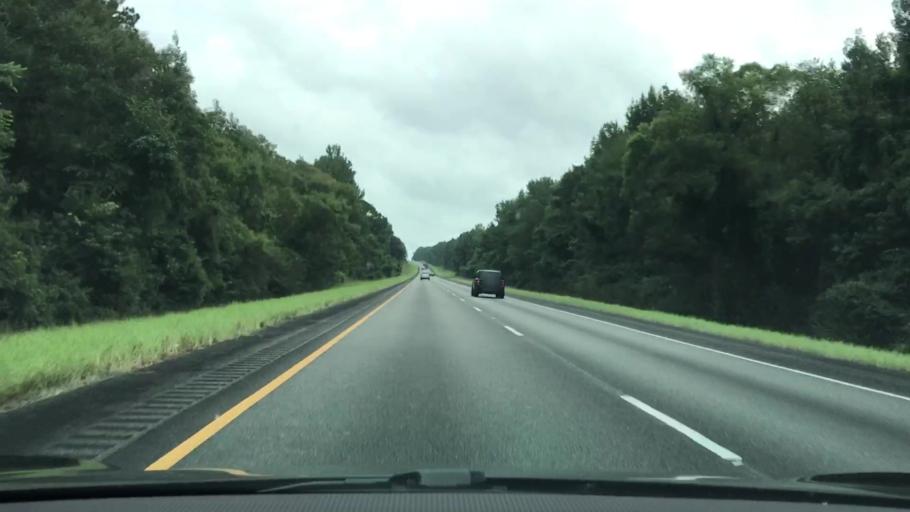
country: US
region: Alabama
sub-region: Elmore County
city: Tallassee
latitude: 32.4386
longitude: -85.8397
